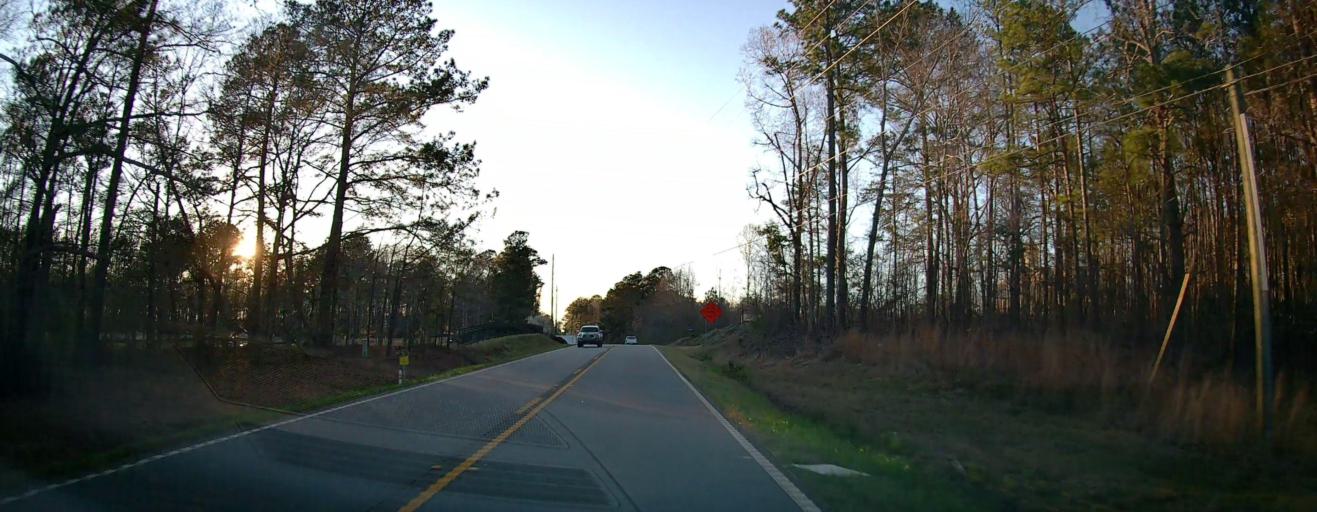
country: US
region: Georgia
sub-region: Harris County
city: Hamilton
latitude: 32.6670
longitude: -84.9646
